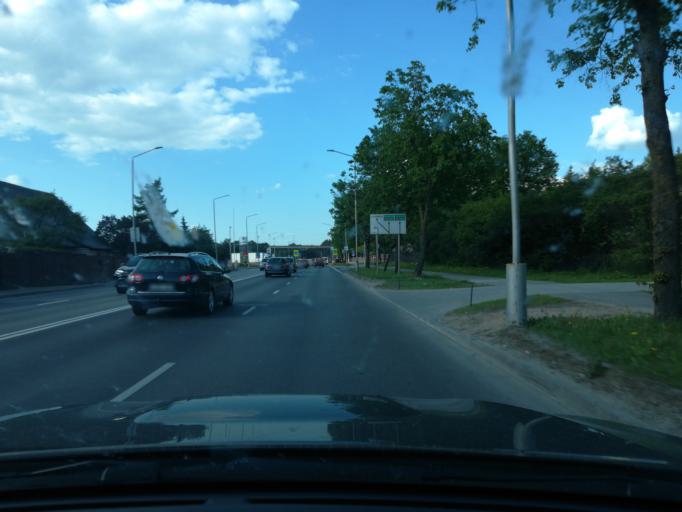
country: LT
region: Kauno apskritis
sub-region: Kaunas
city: Eiguliai
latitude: 54.9330
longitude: 23.9178
